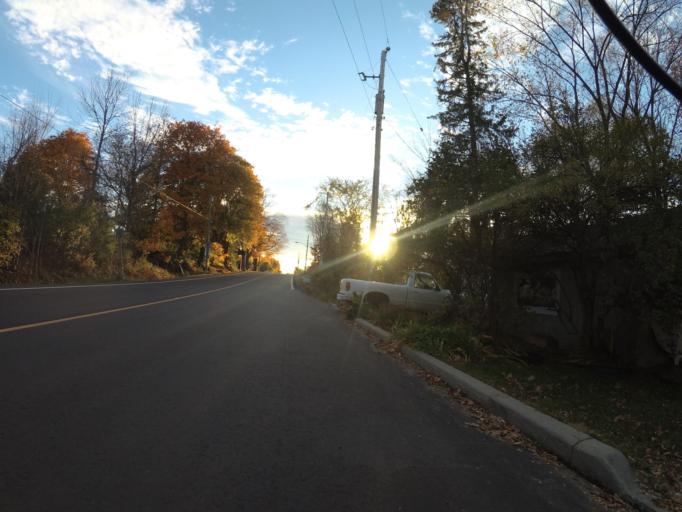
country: CA
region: Ontario
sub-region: Lanark County
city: Smiths Falls
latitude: 44.9674
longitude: -75.8088
